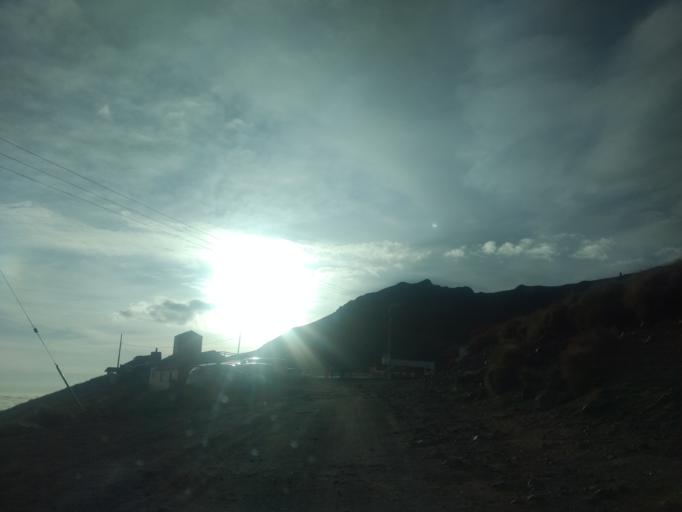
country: MX
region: Mexico
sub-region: Tenango del Valle
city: Santa Cruz Pueblo Nuevo (Pueblo Nuevo)
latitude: 19.1190
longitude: -99.7486
